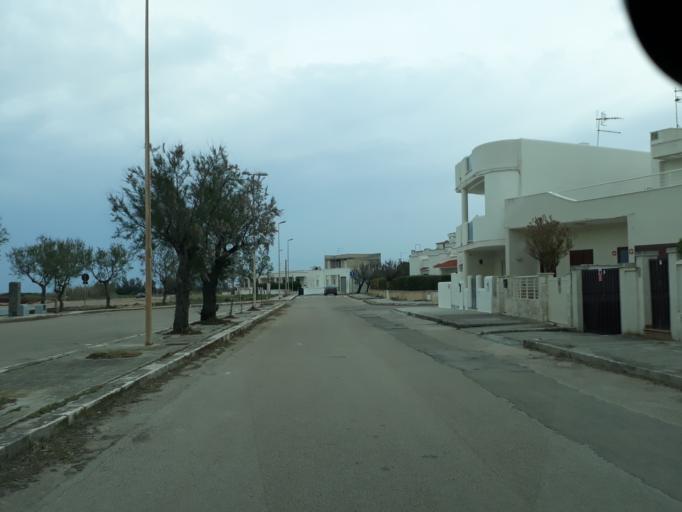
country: IT
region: Apulia
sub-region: Provincia di Brindisi
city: Carovigno
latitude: 40.7565
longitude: 17.7089
